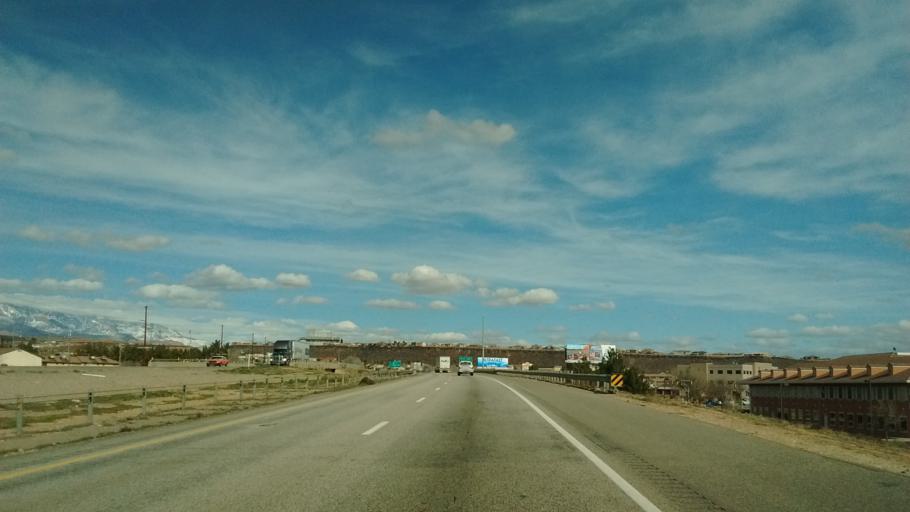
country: US
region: Utah
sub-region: Washington County
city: Saint George
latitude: 37.0953
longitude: -113.5668
